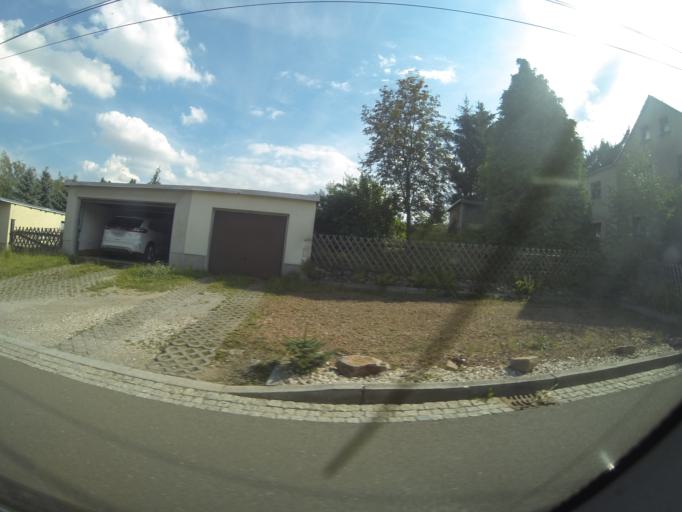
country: DE
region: Thuringia
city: Vollmershain
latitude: 50.8628
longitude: 12.3094
